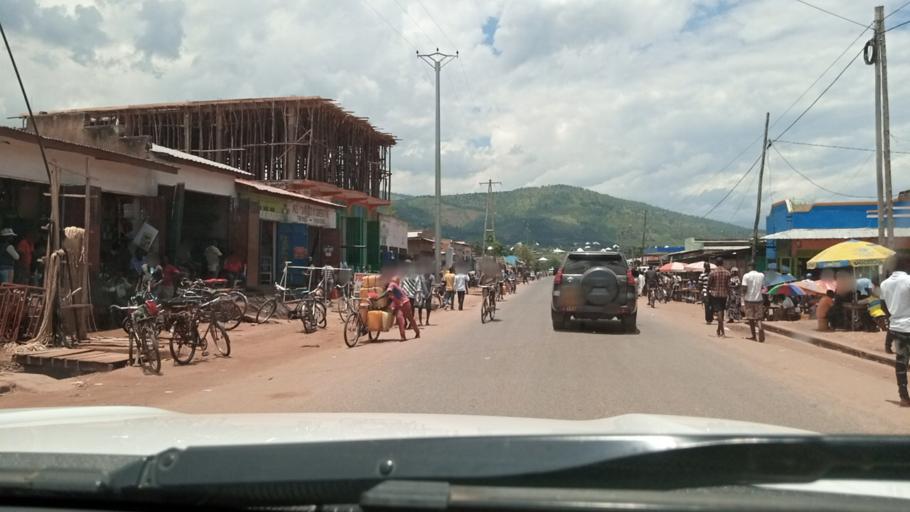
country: BI
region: Bujumbura Mairie
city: Bujumbura
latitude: -3.4743
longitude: 29.3510
